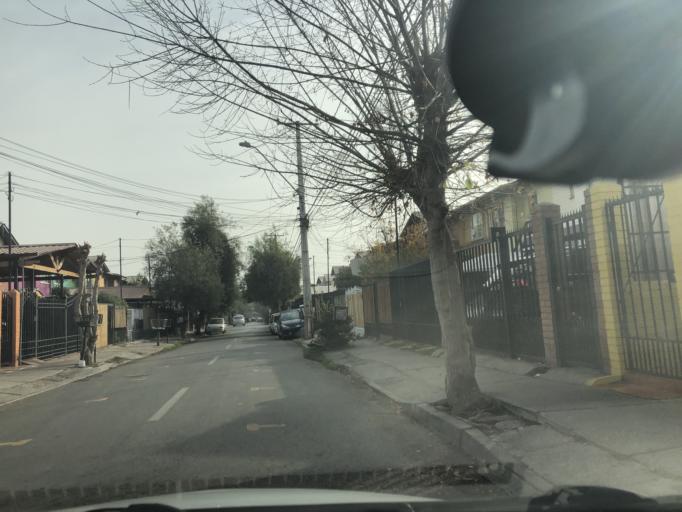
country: CL
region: Santiago Metropolitan
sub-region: Provincia de Cordillera
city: Puente Alto
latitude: -33.5826
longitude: -70.5546
